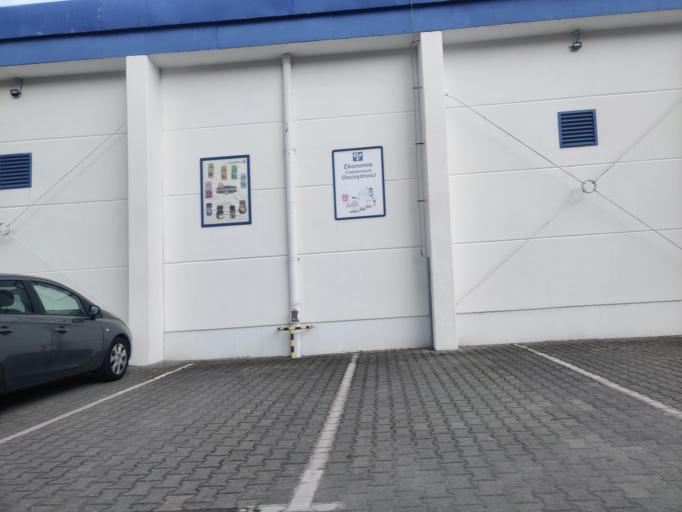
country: PL
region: Greater Poland Voivodeship
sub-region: Konin
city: Konin
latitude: 52.2281
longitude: 18.2729
